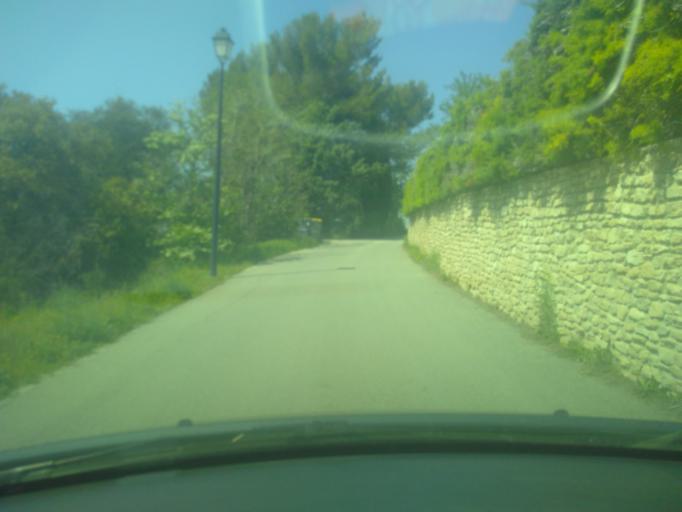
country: FR
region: Provence-Alpes-Cote d'Azur
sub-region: Departement du Vaucluse
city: Venasque
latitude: 43.9919
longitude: 5.1484
